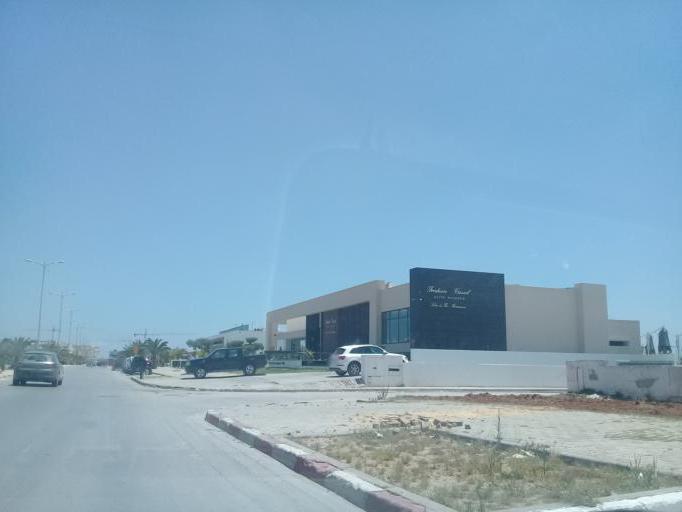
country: TN
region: Tunis
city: La Goulette
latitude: 36.8415
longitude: 10.2681
